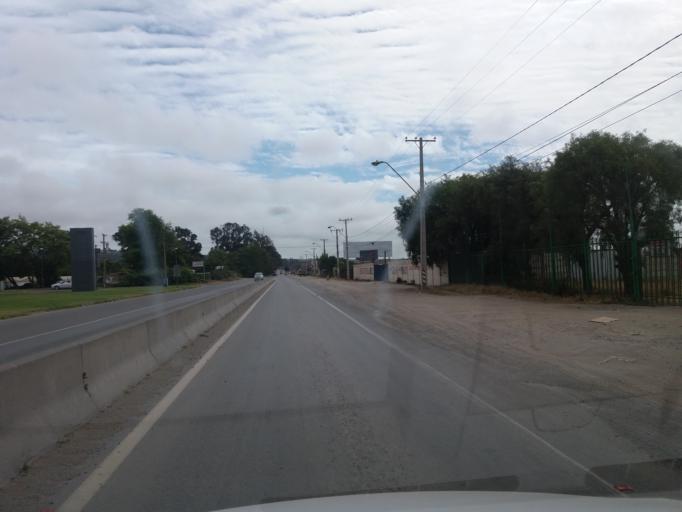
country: CL
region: Valparaiso
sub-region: Provincia de Marga Marga
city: Quilpue
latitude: -32.9285
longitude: -71.4265
